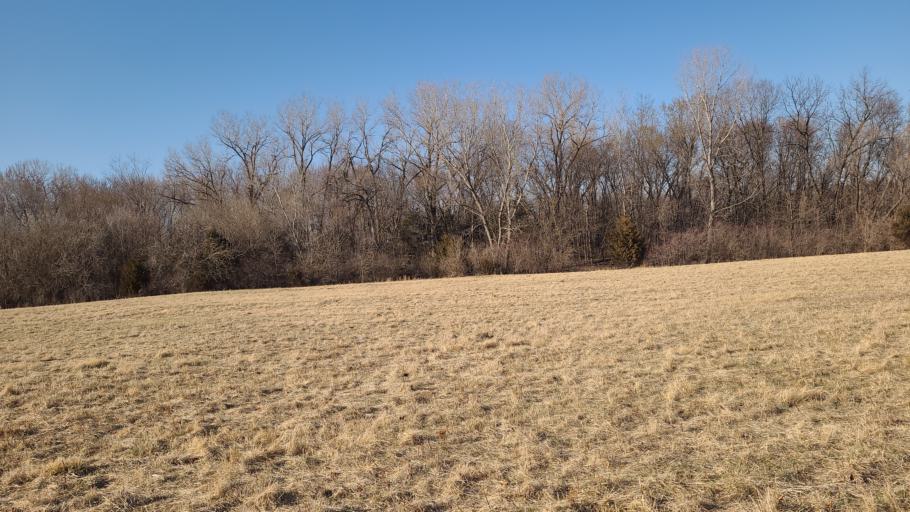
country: US
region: Kansas
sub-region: Douglas County
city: Lawrence
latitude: 38.9870
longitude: -95.2613
